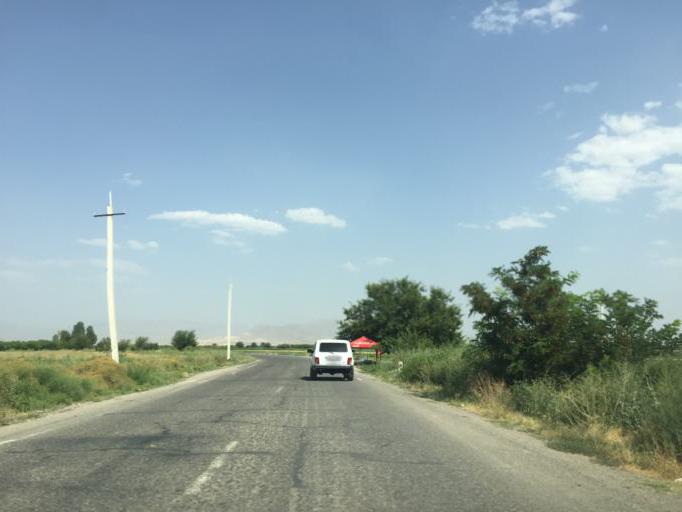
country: AM
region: Ararat
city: Shahumyan
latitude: 39.8828
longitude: 44.5838
